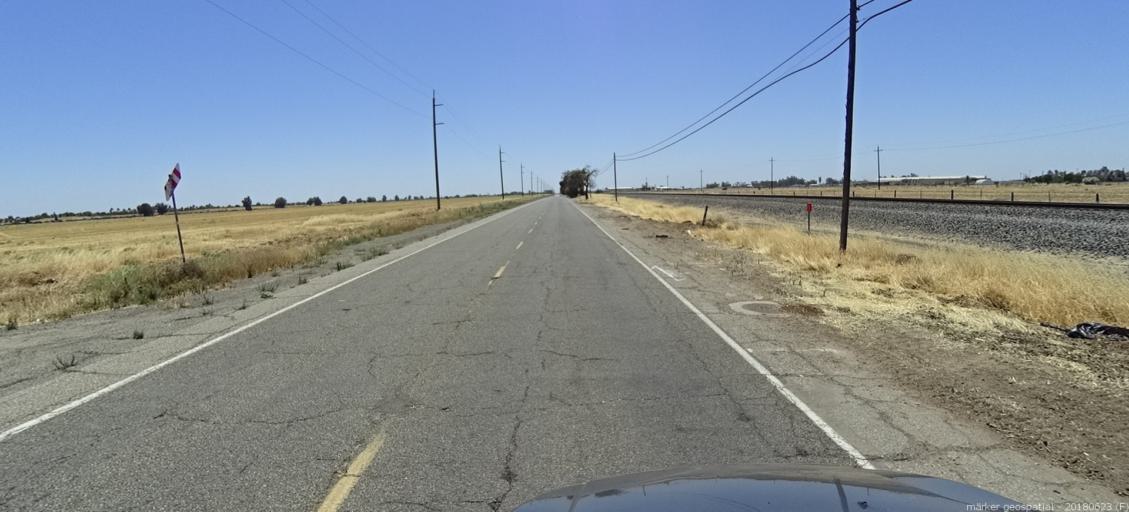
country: US
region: California
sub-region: Madera County
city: Chowchilla
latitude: 37.1175
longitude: -120.2479
